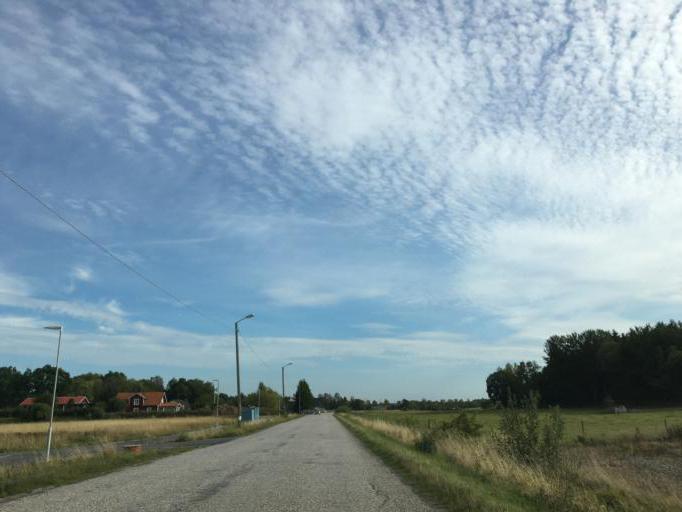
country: SE
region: Soedermanland
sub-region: Eskilstuna Kommun
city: Torshalla
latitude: 59.4411
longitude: 16.4728
